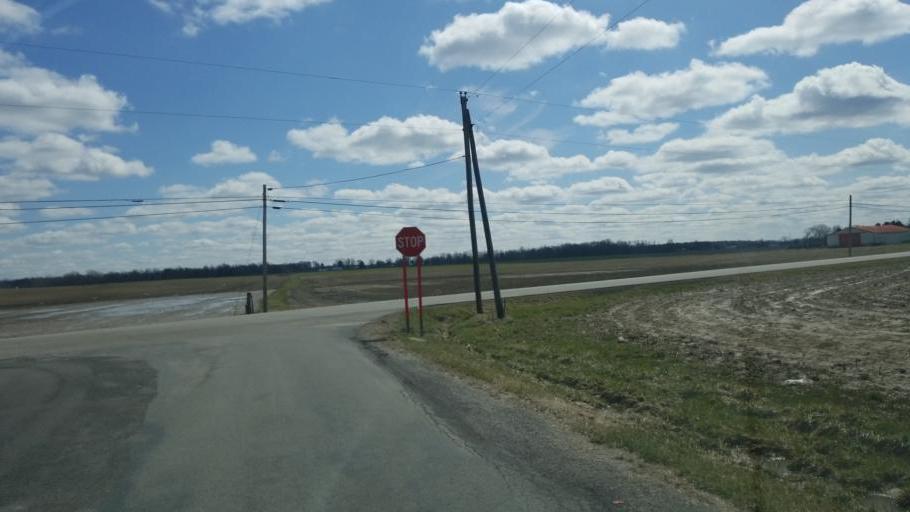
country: US
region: Ohio
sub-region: Richland County
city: Shelby
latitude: 40.8843
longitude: -82.6054
